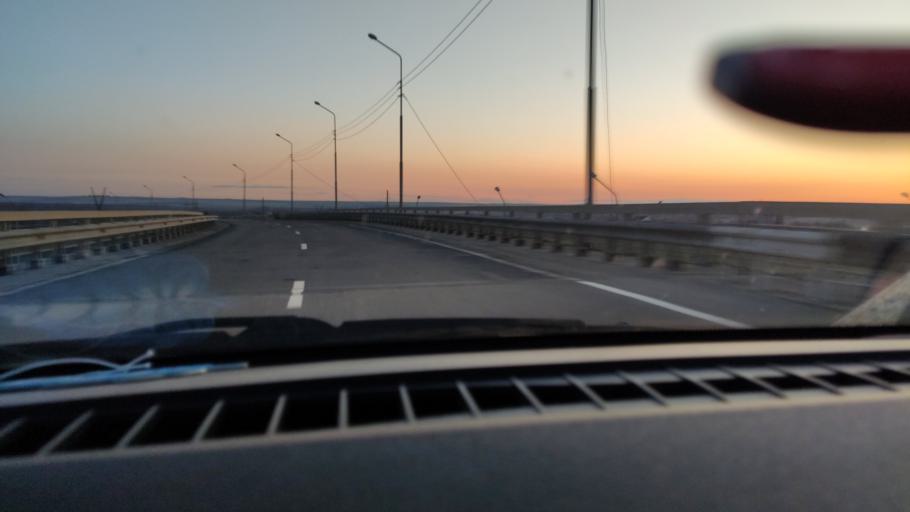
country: RU
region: Saratov
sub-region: Saratovskiy Rayon
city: Saratov
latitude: 51.6679
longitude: 46.0014
